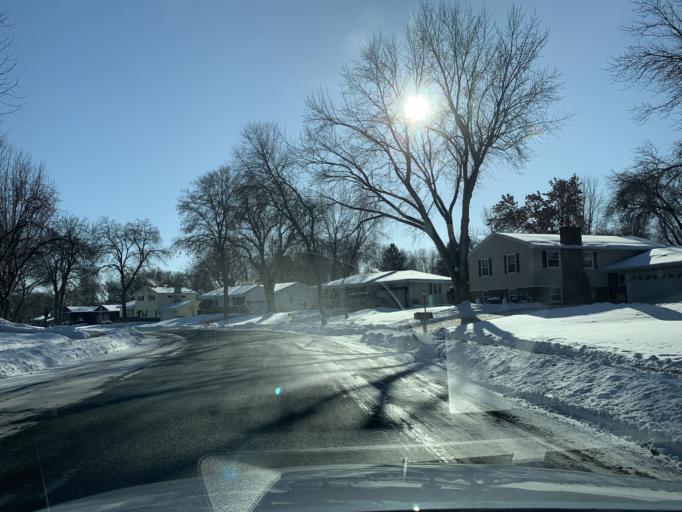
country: US
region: Minnesota
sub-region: Scott County
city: Savage
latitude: 44.8227
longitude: -93.3382
